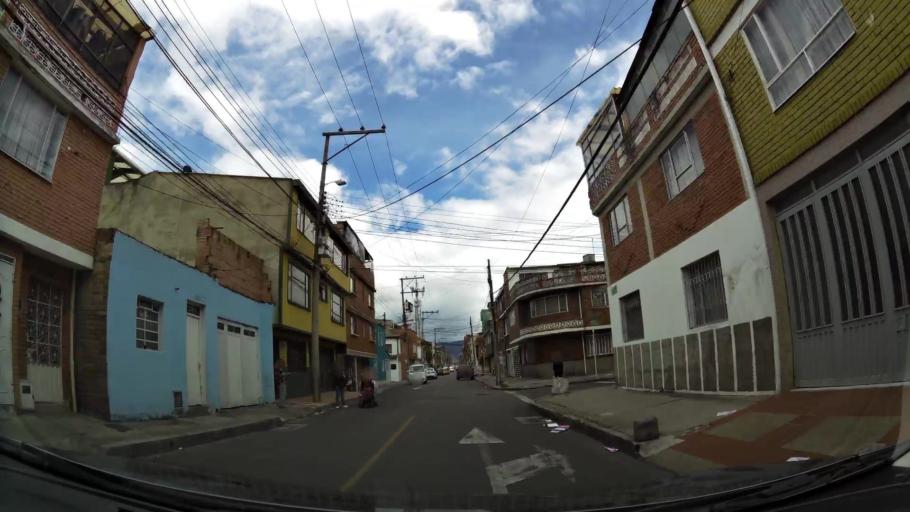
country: CO
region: Bogota D.C.
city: Barrio San Luis
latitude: 4.7066
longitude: -74.0963
